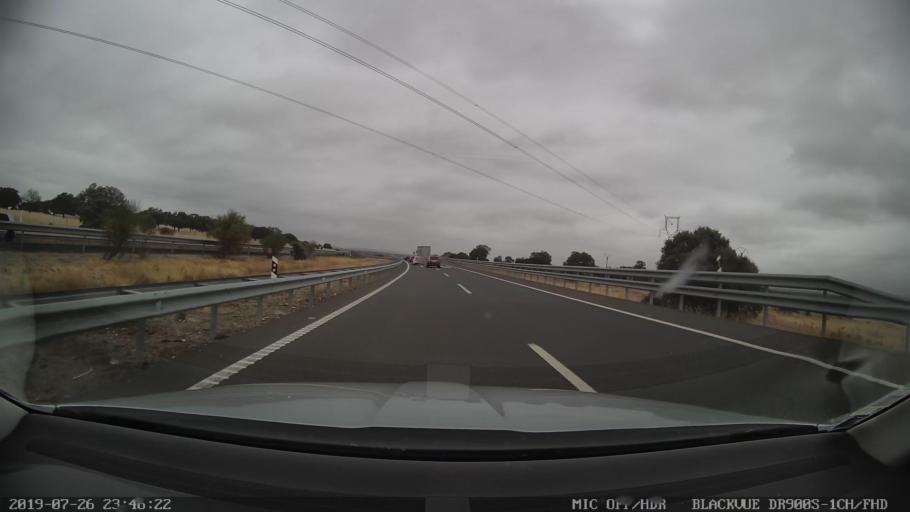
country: ES
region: Extremadura
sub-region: Provincia de Caceres
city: Jaraicejo
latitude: 39.5874
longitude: -5.8352
